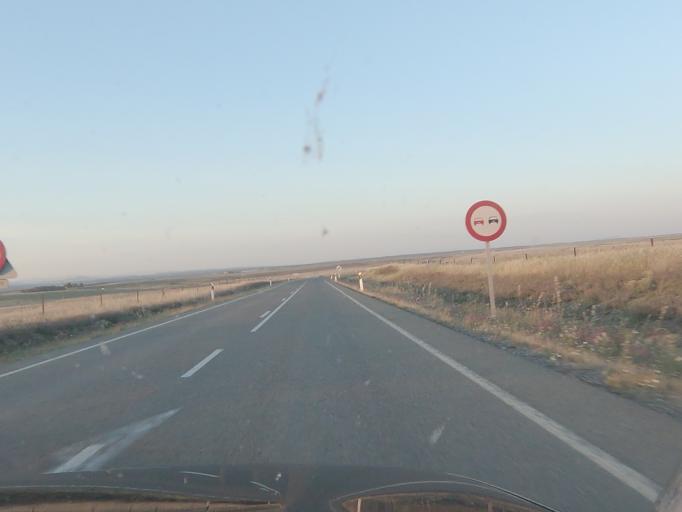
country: ES
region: Extremadura
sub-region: Provincia de Caceres
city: Alcantara
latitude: 39.6250
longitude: -6.9330
